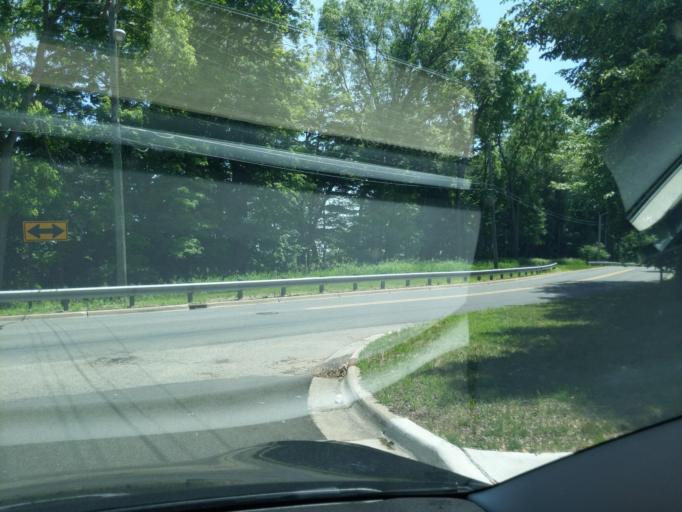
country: US
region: Michigan
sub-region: Muskegon County
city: Montague
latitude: 43.4144
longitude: -86.3600
